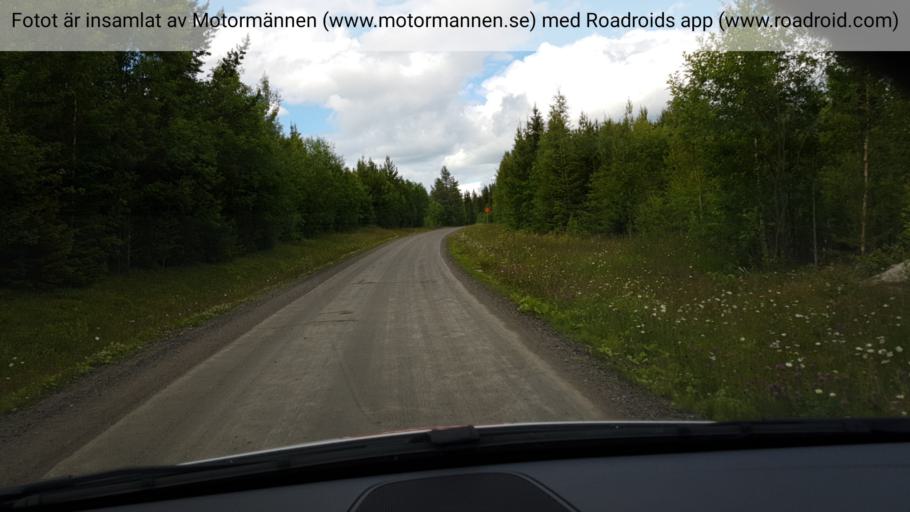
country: SE
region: Jaemtland
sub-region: Stroemsunds Kommun
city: Stroemsund
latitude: 64.0186
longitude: 15.9314
